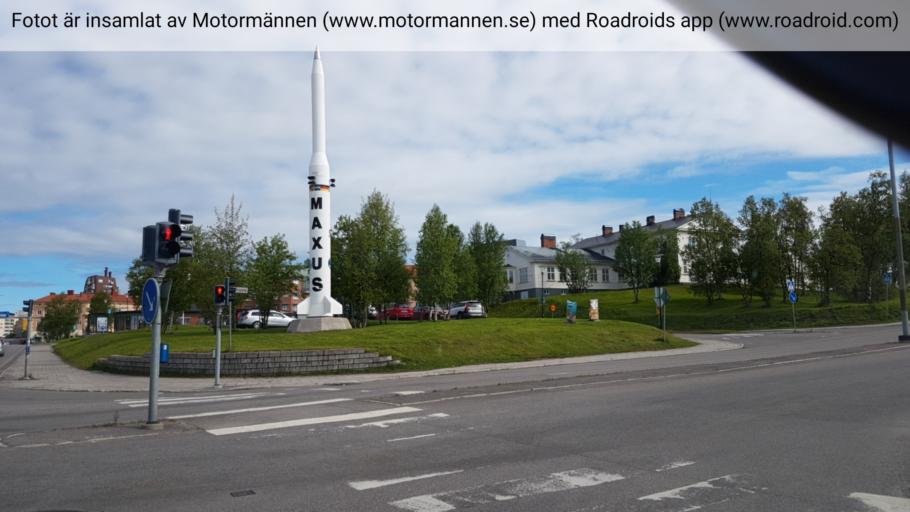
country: SE
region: Norrbotten
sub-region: Kiruna Kommun
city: Kiruna
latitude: 67.8509
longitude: 20.2246
